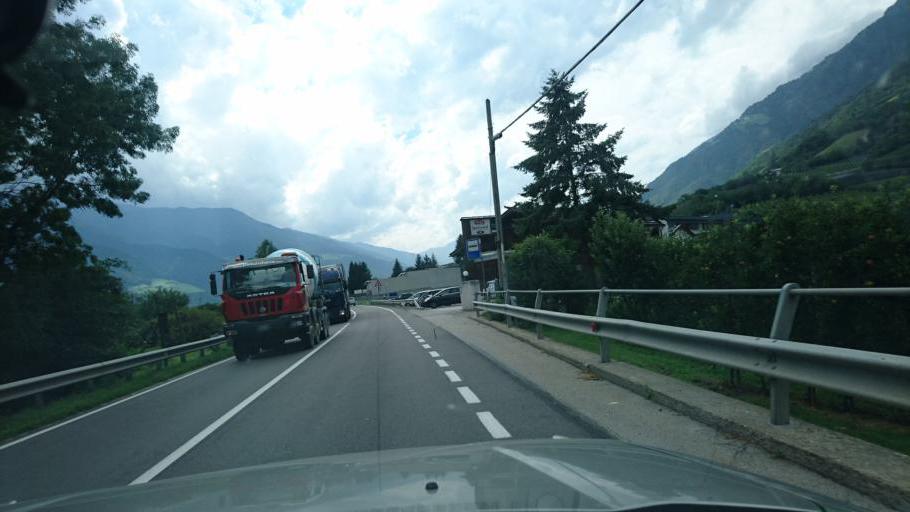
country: IT
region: Trentino-Alto Adige
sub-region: Bolzano
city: Plaus
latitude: 46.6572
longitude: 11.0294
